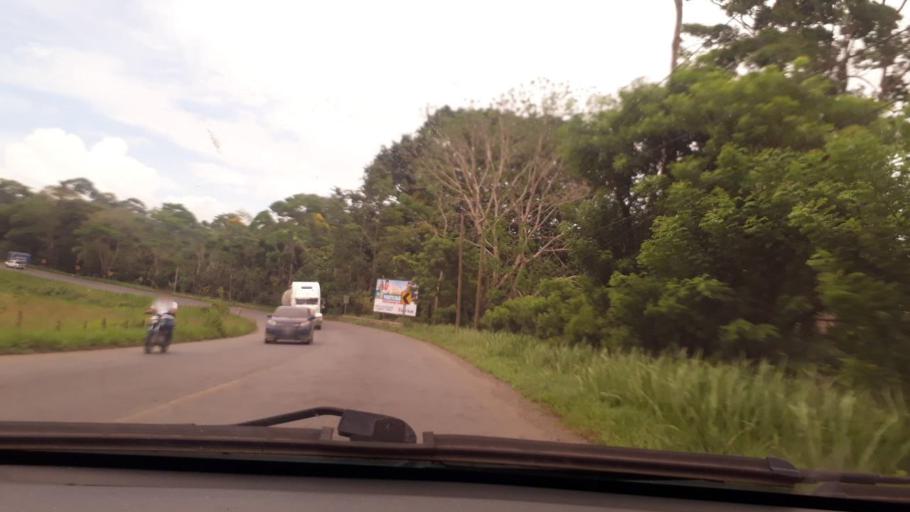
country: GT
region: Izabal
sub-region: Municipio de Puerto Barrios
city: Puerto Barrios
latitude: 15.6204
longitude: -88.5603
